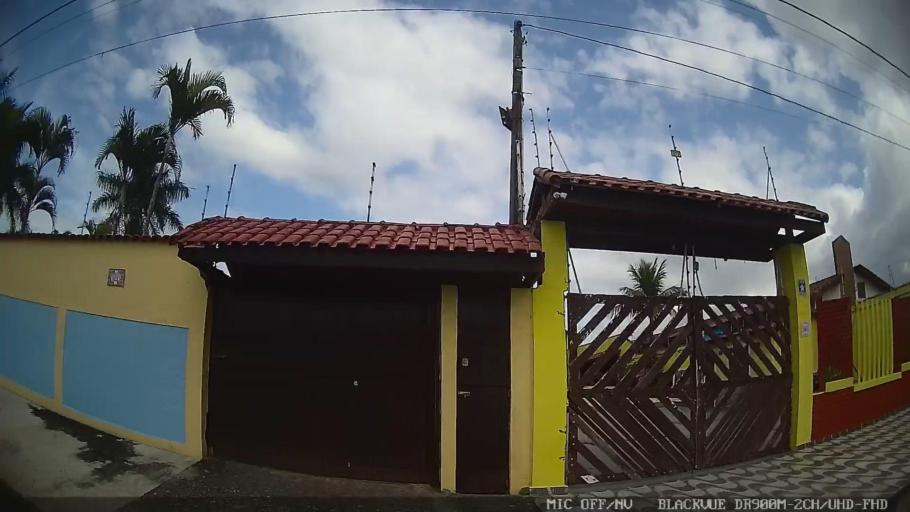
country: BR
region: Sao Paulo
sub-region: Itanhaem
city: Itanhaem
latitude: -24.2032
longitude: -46.8416
